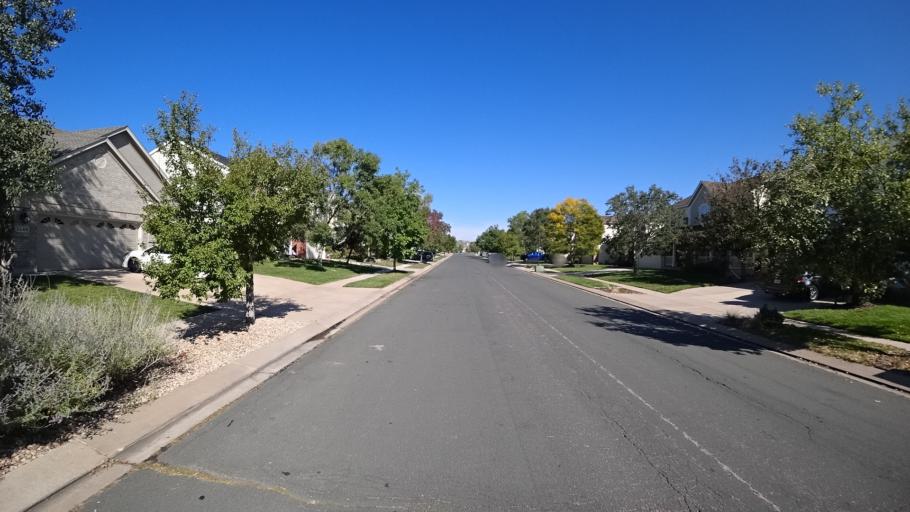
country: US
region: Colorado
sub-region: El Paso County
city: Cimarron Hills
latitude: 38.8818
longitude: -104.7078
